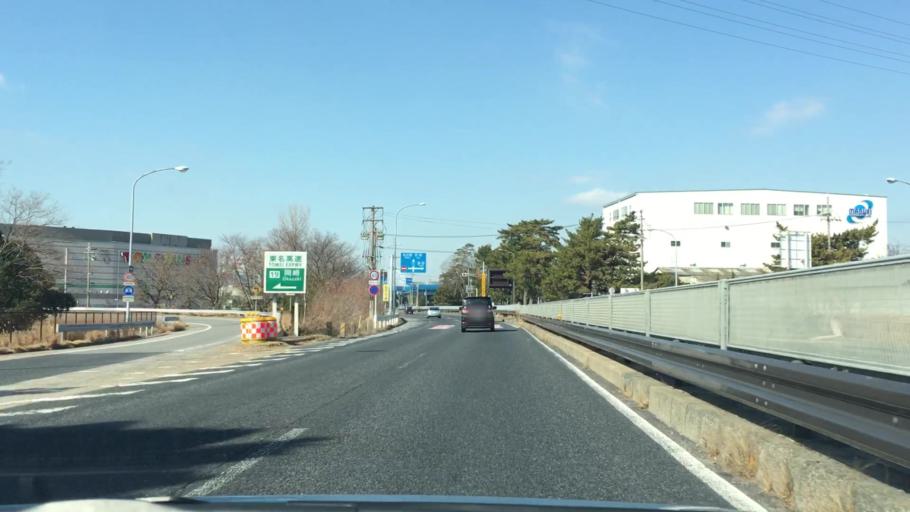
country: JP
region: Aichi
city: Okazaki
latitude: 34.9452
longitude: 137.1894
